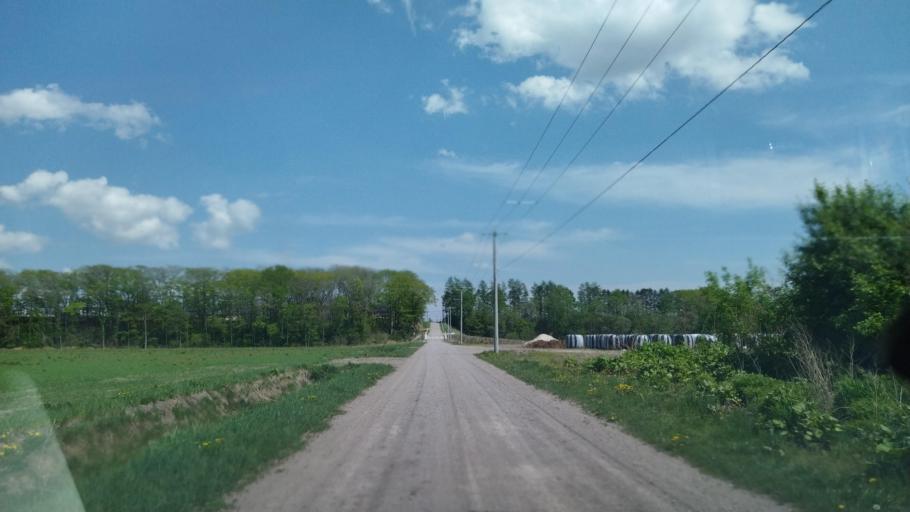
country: JP
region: Hokkaido
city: Otofuke
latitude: 43.1321
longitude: 143.2193
